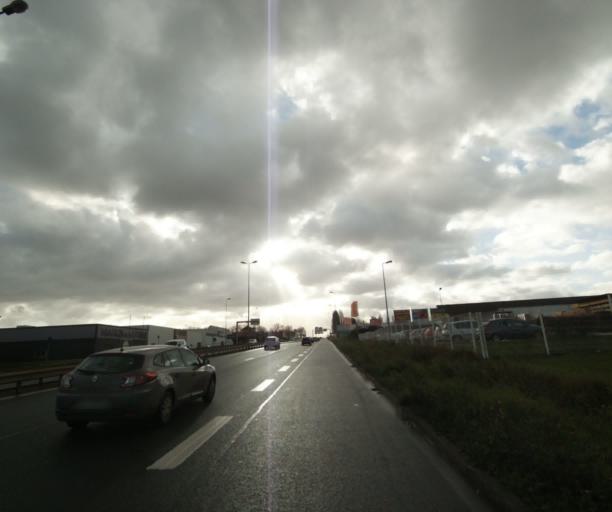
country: FR
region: Pays de la Loire
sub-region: Departement de la Sarthe
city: La Chapelle-Saint-Aubin
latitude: 48.0359
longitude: 0.1764
